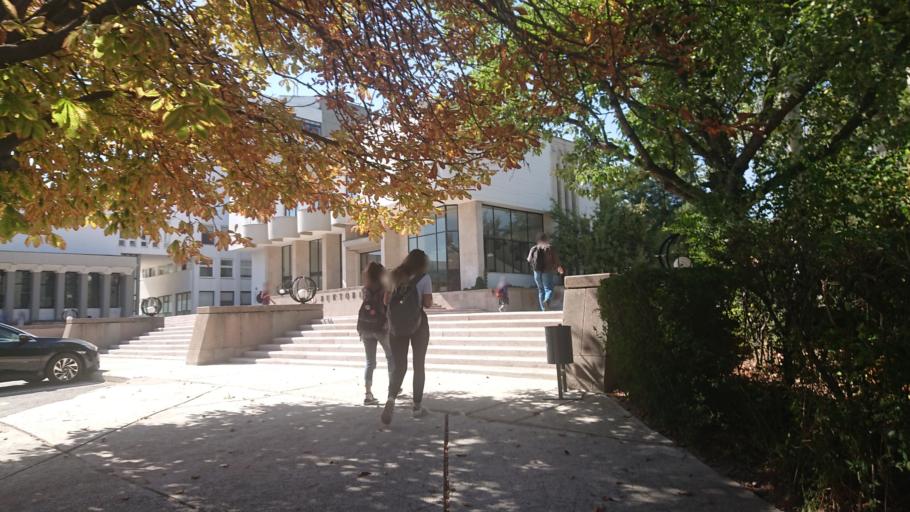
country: TR
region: Ankara
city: Ankara
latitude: 39.8953
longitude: 32.7843
